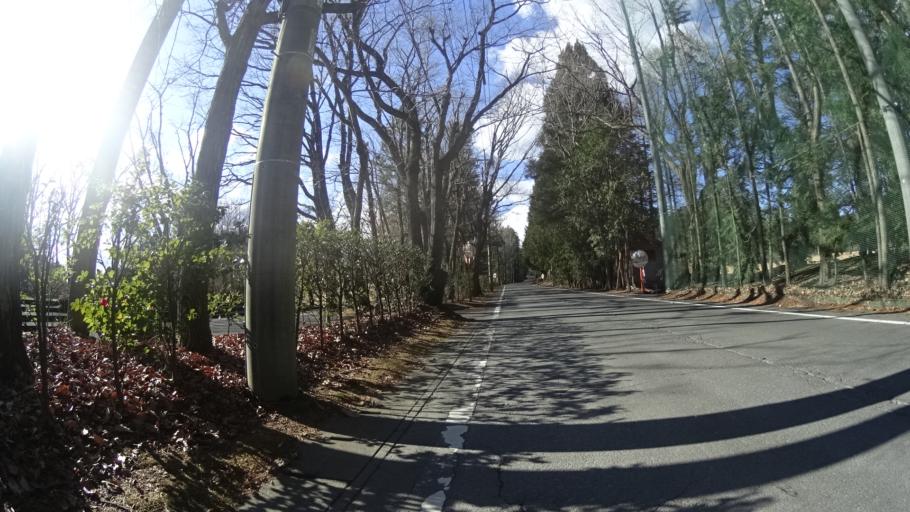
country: JP
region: Shizuoka
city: Gotemba
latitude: 35.3440
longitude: 138.8942
